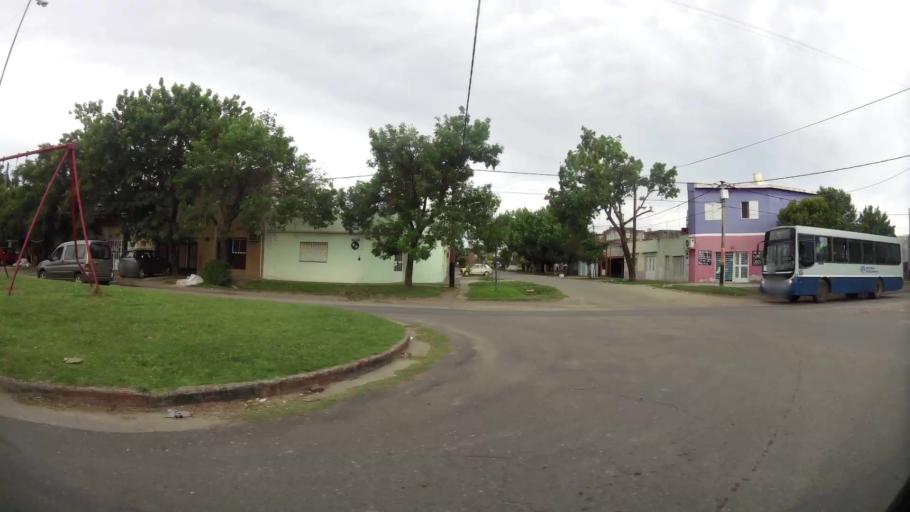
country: AR
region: Santa Fe
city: Gobernador Galvez
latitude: -32.9995
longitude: -60.6779
